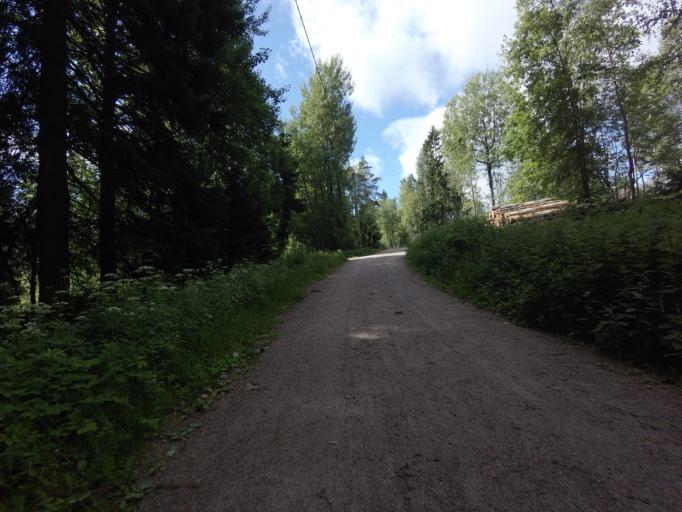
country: FI
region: Uusimaa
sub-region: Helsinki
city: Espoo
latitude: 60.1791
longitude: 24.6451
